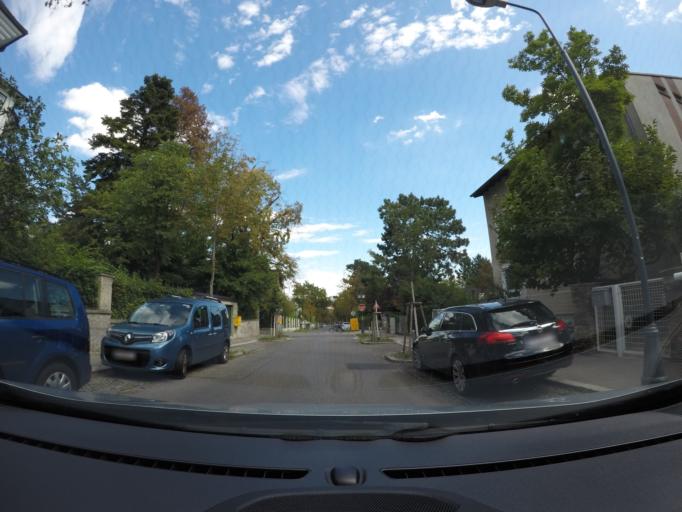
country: AT
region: Lower Austria
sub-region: Politischer Bezirk Modling
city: Perchtoldsdorf
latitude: 48.1799
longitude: 16.2753
